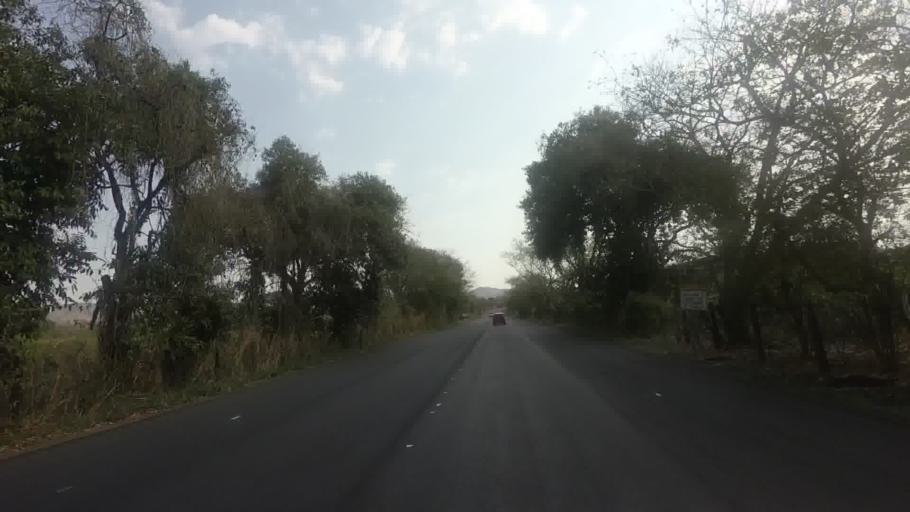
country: BR
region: Rio de Janeiro
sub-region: Bom Jesus Do Itabapoana
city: Bom Jesus do Itabapoana
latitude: -21.1917
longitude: -41.6945
